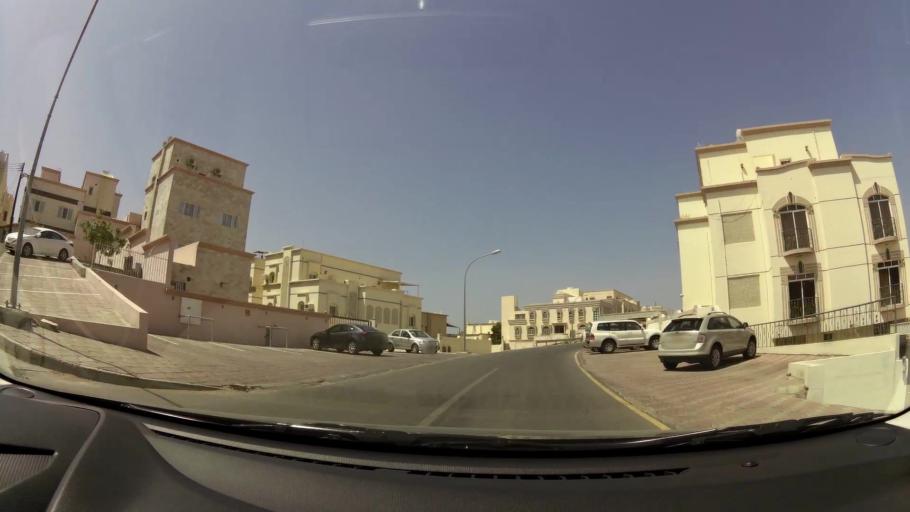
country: OM
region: Muhafazat Masqat
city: Muscat
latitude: 23.6177
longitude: 58.5080
